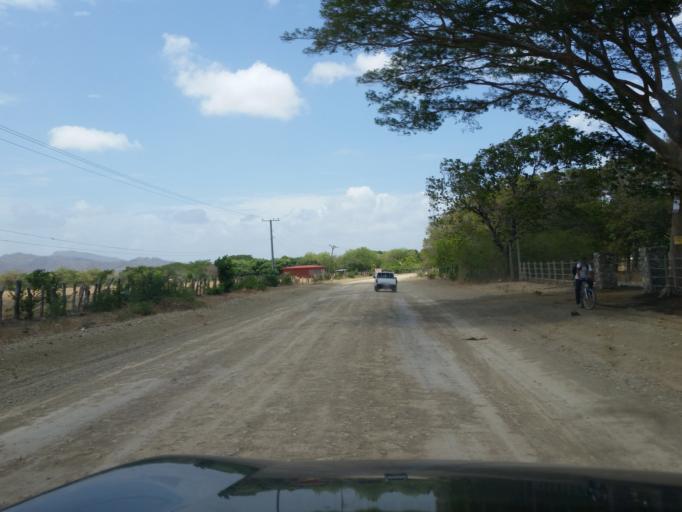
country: NI
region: Rivas
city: Tola
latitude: 11.4647
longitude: -86.0842
